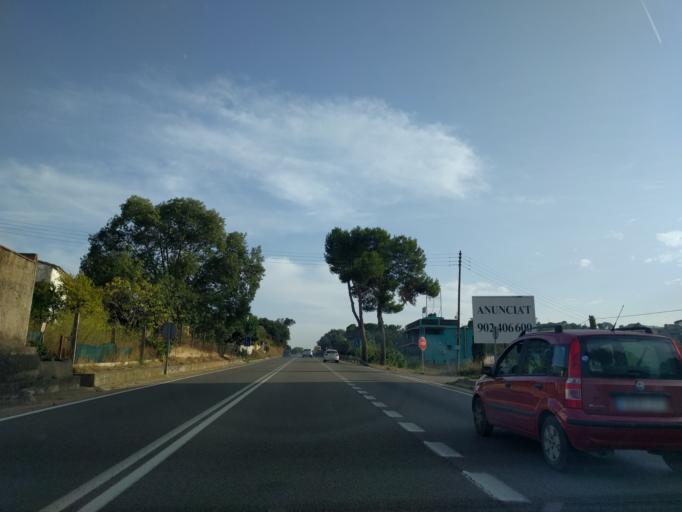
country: ES
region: Catalonia
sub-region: Provincia de Barcelona
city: Tordera
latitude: 41.6905
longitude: 2.7227
